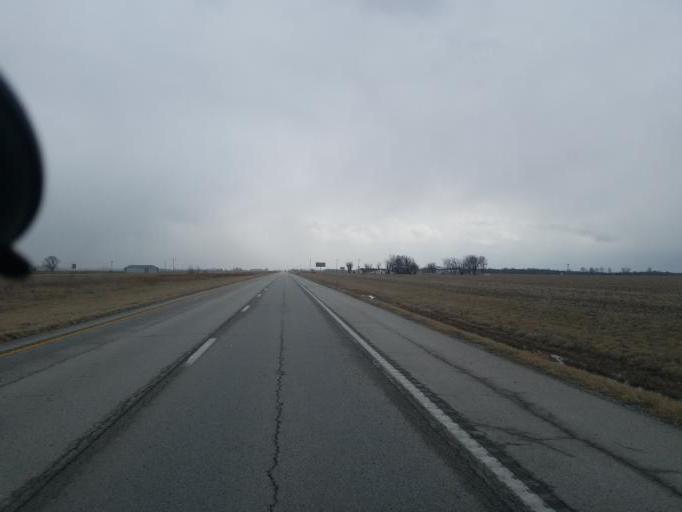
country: US
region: Missouri
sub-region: Randolph County
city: Moberly
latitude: 39.5668
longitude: -92.4626
